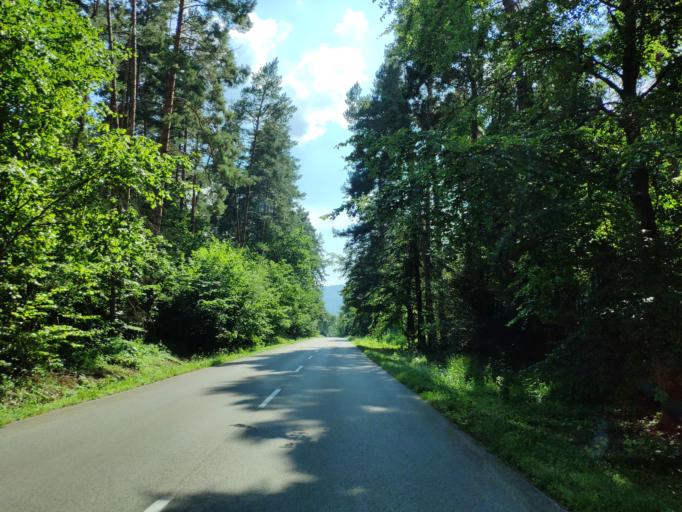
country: SK
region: Kosicky
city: Dobsina
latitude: 48.7043
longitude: 20.3601
